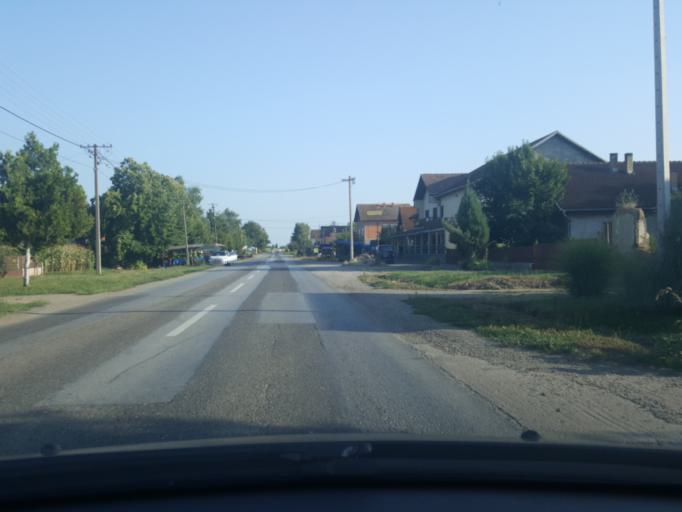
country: RS
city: Hrtkovci
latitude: 44.8712
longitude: 19.7700
